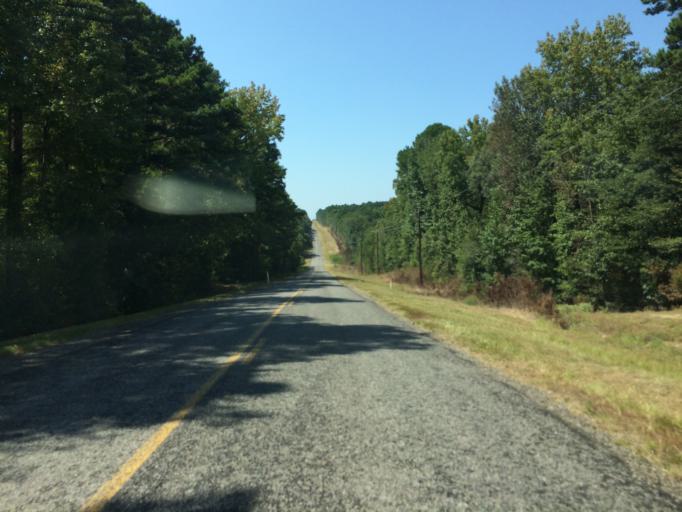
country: US
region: Texas
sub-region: Wood County
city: Hawkins
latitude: 32.7312
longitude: -95.1993
